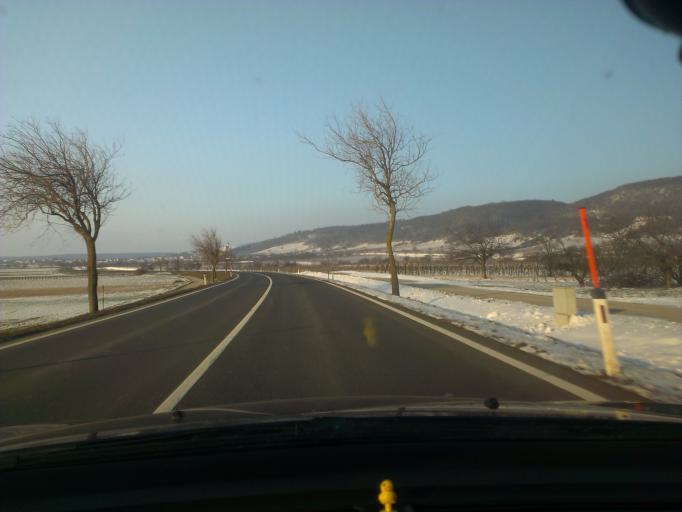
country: AT
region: Burgenland
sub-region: Eisenstadt-Umgebung
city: Donnerskirchen
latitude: 47.9071
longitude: 16.6630
